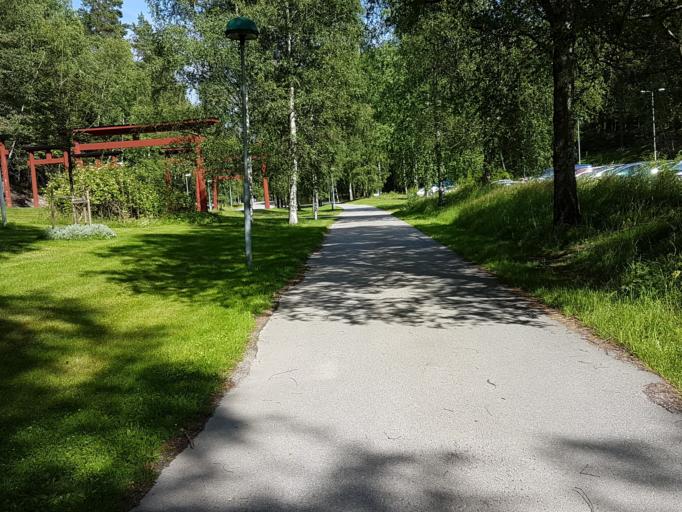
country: SE
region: Stockholm
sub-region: Lidingo
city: Brevik
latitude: 59.3441
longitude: 18.2404
